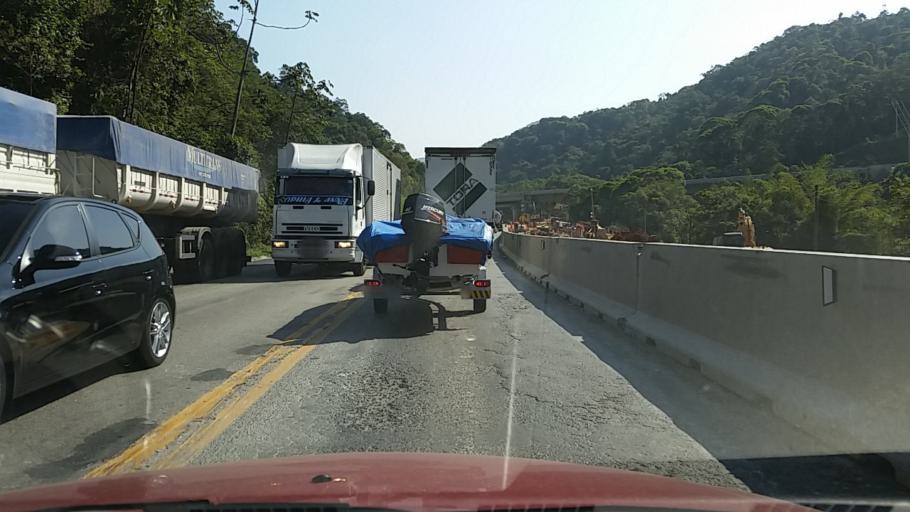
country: BR
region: Sao Paulo
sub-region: Juquitiba
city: Juquitiba
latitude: -24.0705
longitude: -47.2430
